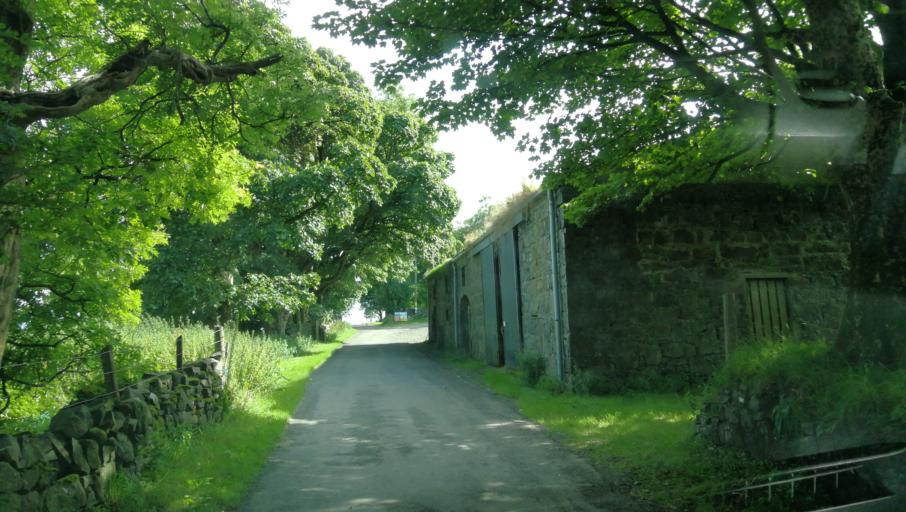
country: GB
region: Scotland
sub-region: Highland
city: Isle of Skye
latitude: 57.3966
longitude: -6.5673
